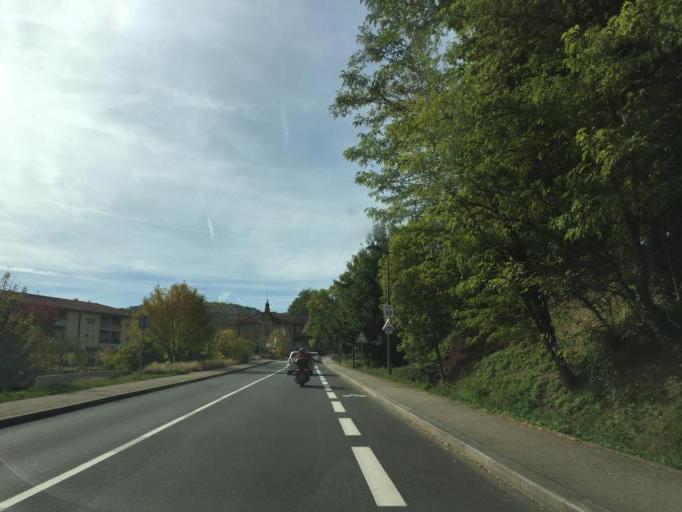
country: FR
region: Rhone-Alpes
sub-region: Departement du Rhone
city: Chasselay
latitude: 45.8850
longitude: 4.8031
